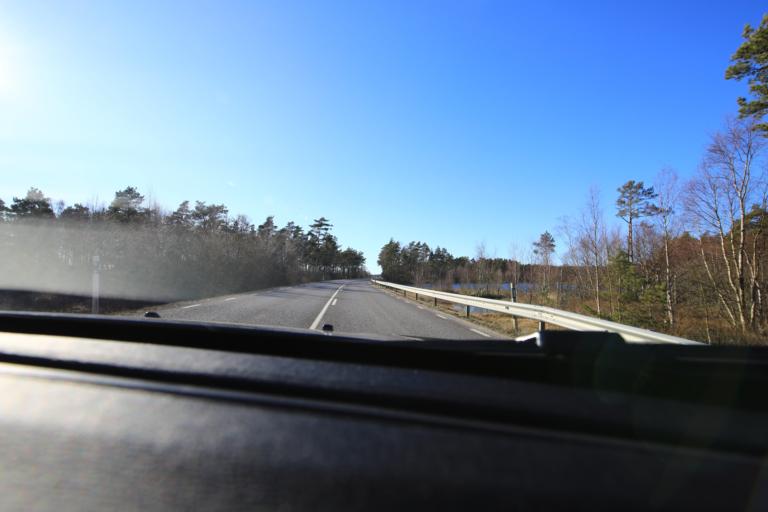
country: SE
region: Halland
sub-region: Varbergs Kommun
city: Tvaaker
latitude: 57.0478
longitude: 12.3566
